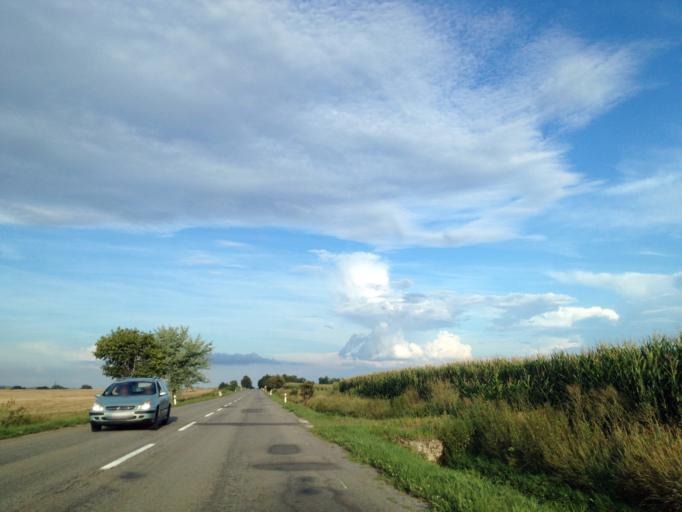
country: SK
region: Nitriansky
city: Svodin
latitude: 47.9023
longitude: 18.3509
